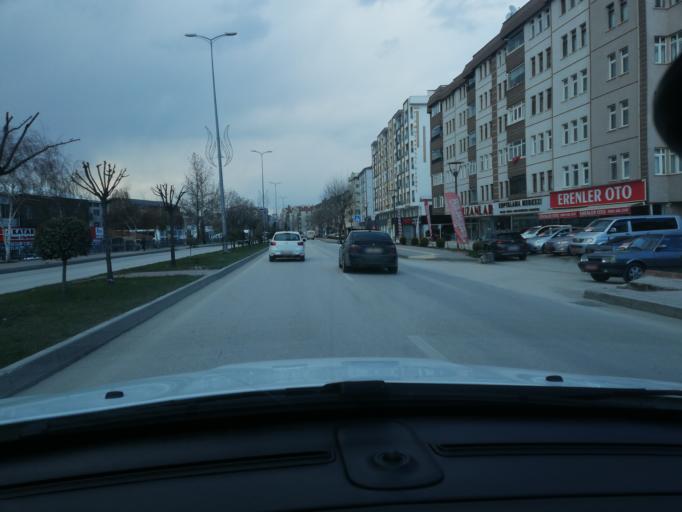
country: TR
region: Kastamonu
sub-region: Cide
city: Kastamonu
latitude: 41.3929
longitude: 33.7817
